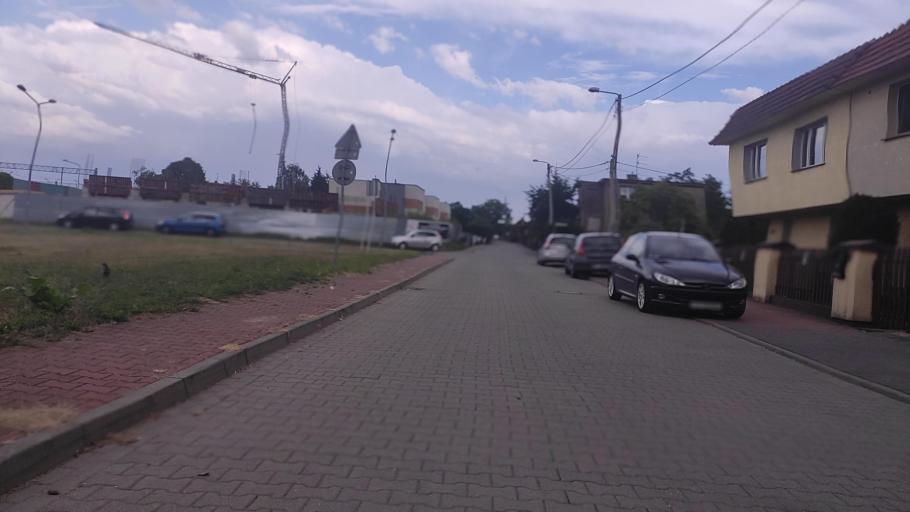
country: PL
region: Greater Poland Voivodeship
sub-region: Powiat poznanski
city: Swarzedz
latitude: 52.4034
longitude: 17.0749
